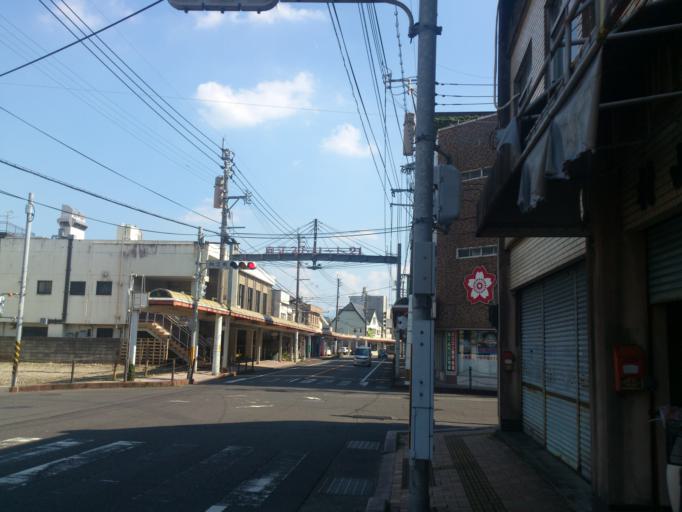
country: JP
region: Kagoshima
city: Kanoya
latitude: 31.3857
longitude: 130.8505
